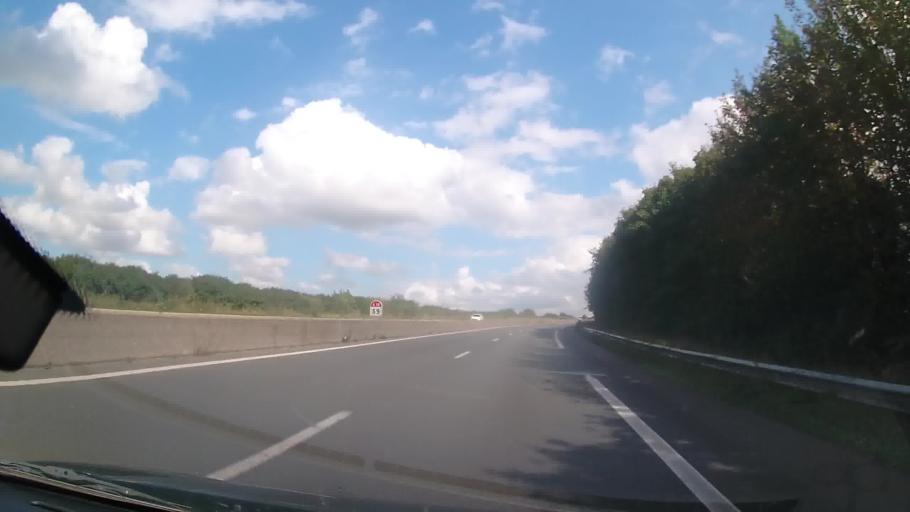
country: FR
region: Nord-Pas-de-Calais
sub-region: Departement du Pas-de-Calais
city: Wimille
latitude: 50.7854
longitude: 1.6617
